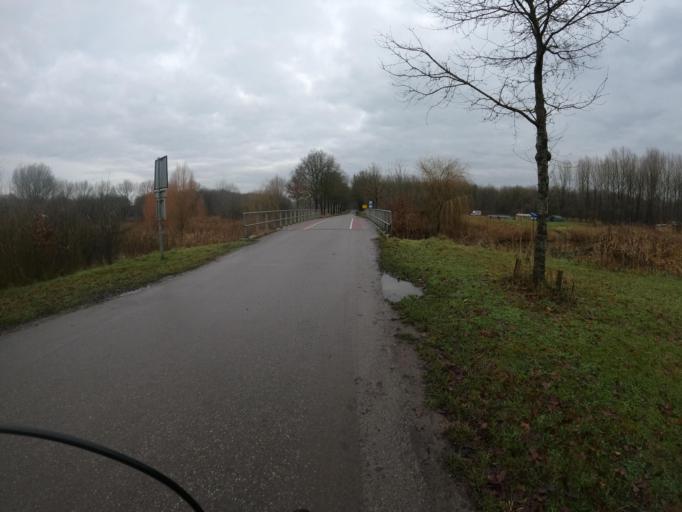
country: NL
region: Flevoland
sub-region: Gemeente Zeewolde
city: Zeewolde
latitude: 52.3333
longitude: 5.4962
